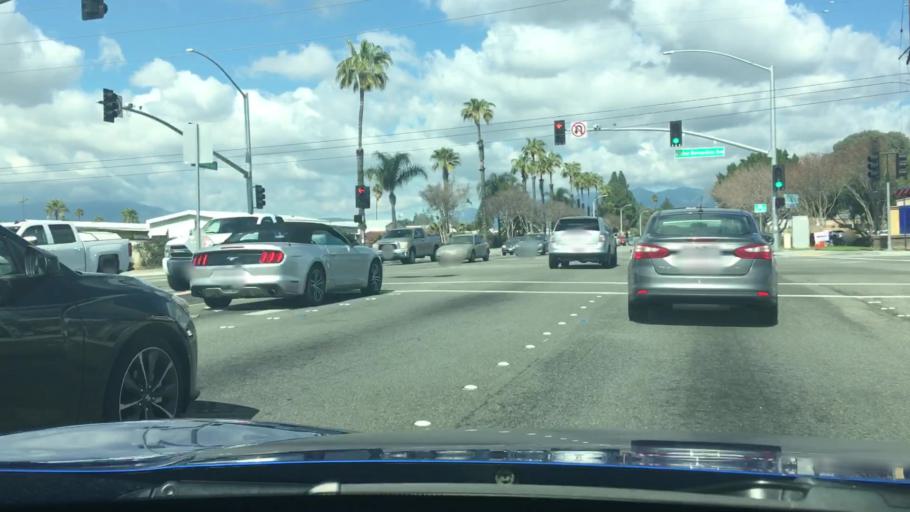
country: US
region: California
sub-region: San Bernardino County
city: Bloomington
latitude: 34.0775
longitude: -117.3702
